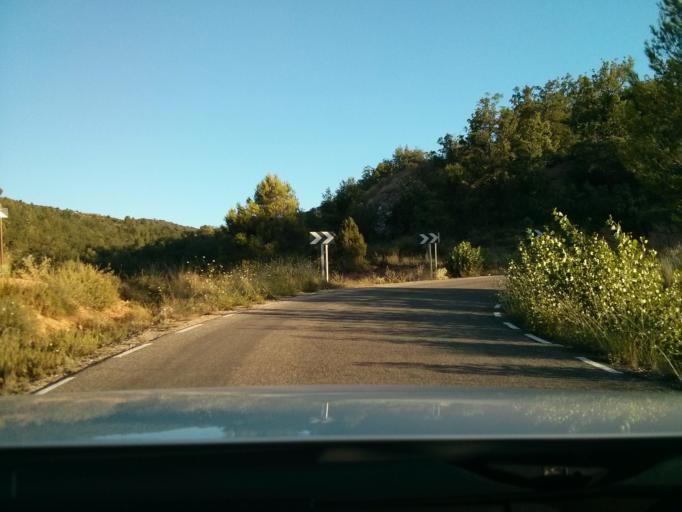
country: ES
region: Castille-La Mancha
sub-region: Provincia de Guadalajara
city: Mantiel
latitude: 40.6323
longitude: -2.6409
